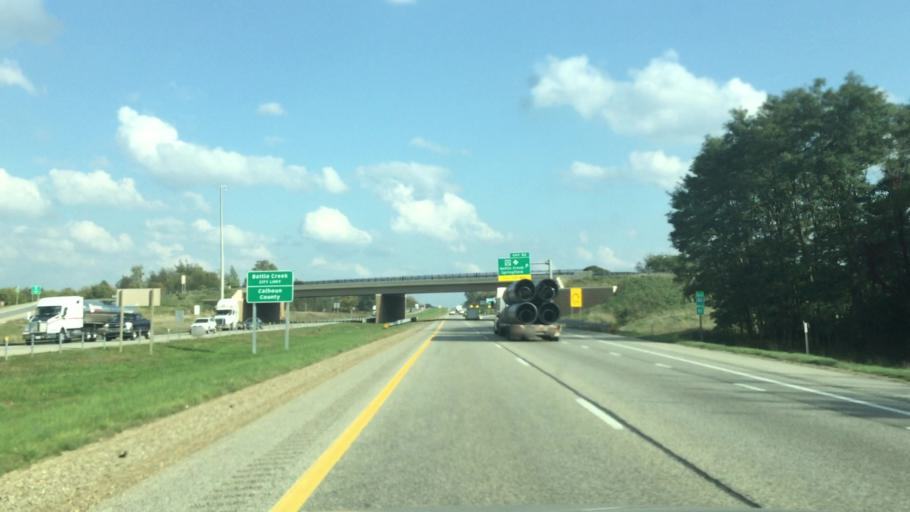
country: US
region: Michigan
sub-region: Calhoun County
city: Springfield
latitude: 42.2729
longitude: -85.2978
